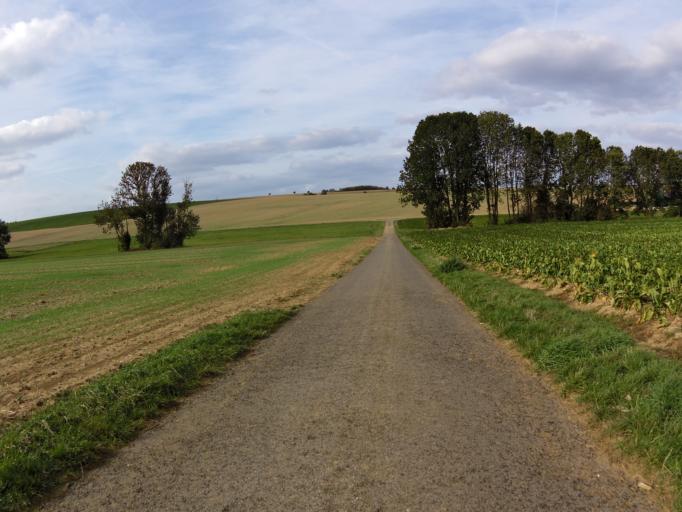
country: DE
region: Bavaria
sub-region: Regierungsbezirk Unterfranken
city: Eibelstadt
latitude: 49.7077
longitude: 9.9588
